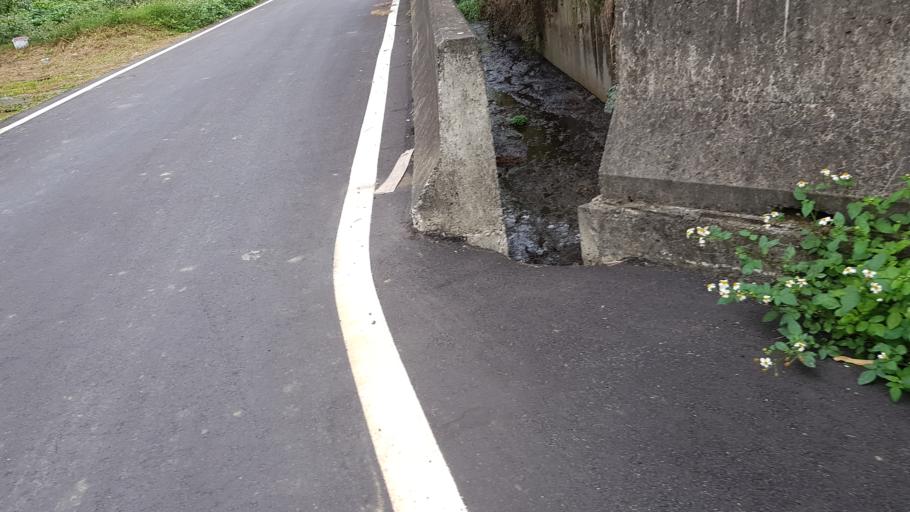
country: TW
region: Taiwan
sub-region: Hsinchu
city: Hsinchu
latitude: 24.7632
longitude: 120.9548
